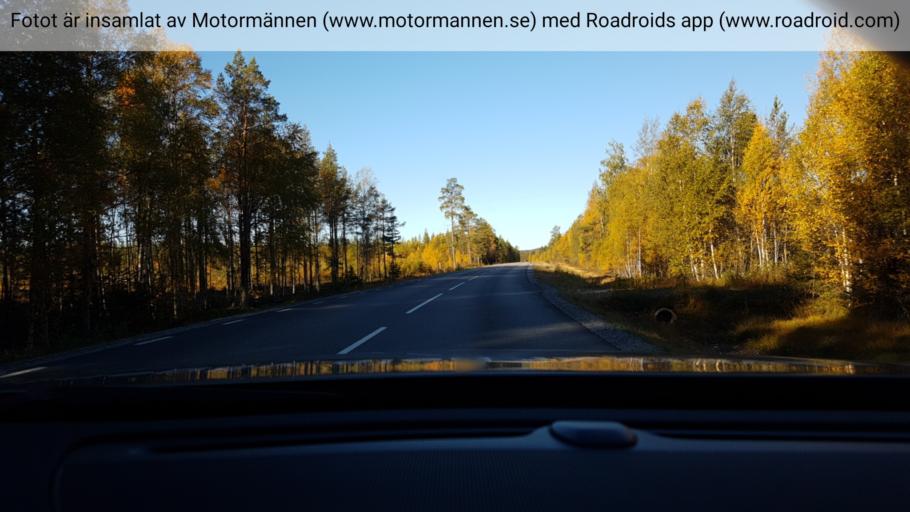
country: SE
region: Norrbotten
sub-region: Pitea Kommun
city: Roknas
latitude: 65.3416
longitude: 20.9706
